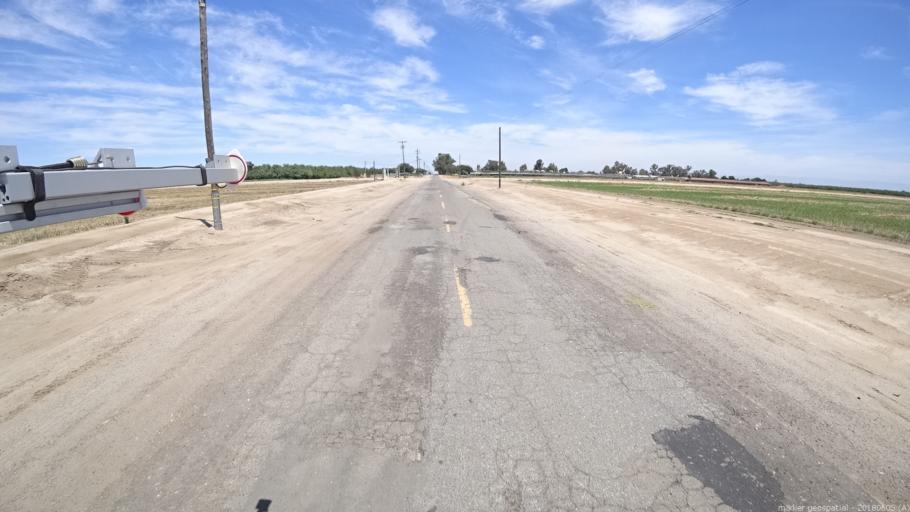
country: US
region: California
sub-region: Madera County
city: Chowchilla
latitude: 37.1080
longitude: -120.3652
